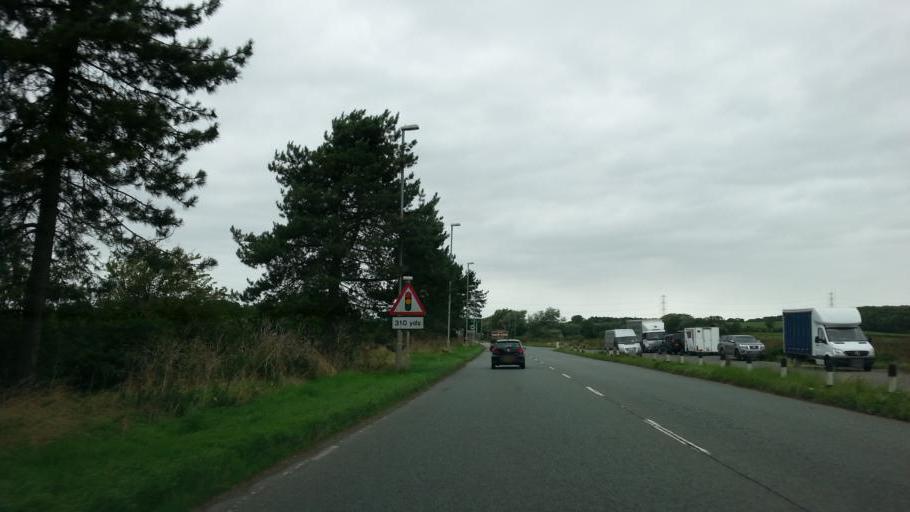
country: GB
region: England
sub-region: Nottinghamshire
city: Farndon
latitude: 53.0881
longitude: -0.8720
